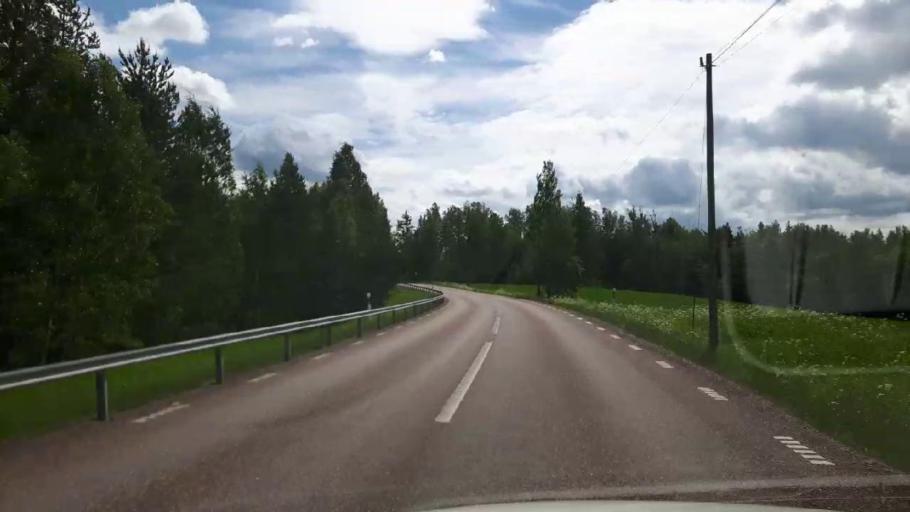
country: SE
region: Dalarna
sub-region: Saters Kommun
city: Saeter
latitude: 60.4157
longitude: 15.8483
